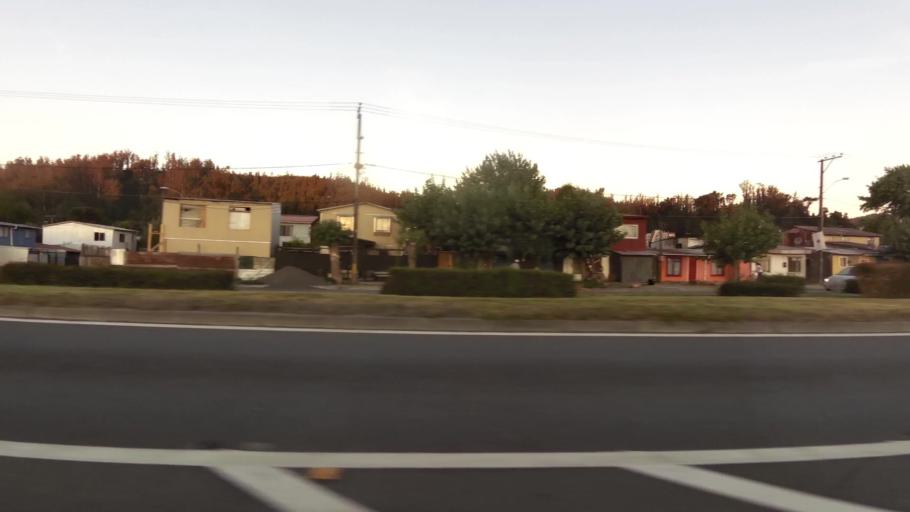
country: CL
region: Biobio
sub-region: Provincia de Concepcion
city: Concepcion
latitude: -36.8440
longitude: -73.0566
